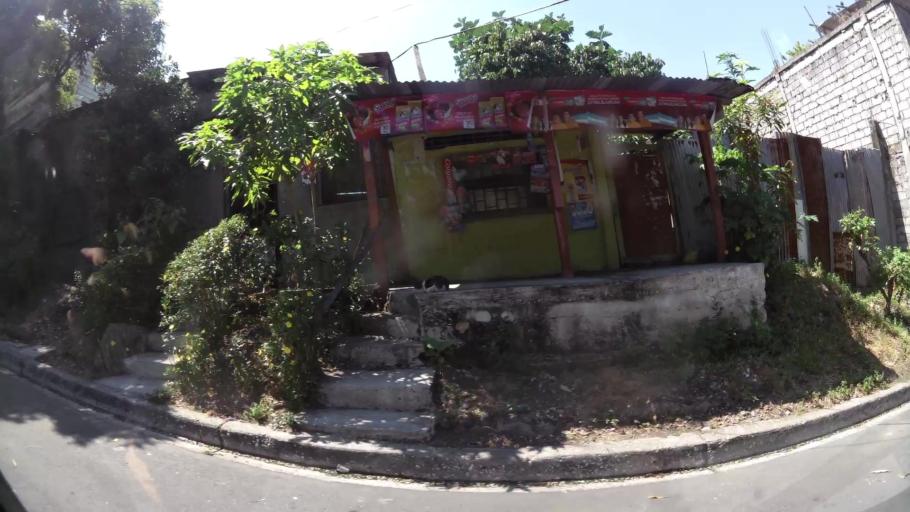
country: EC
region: Guayas
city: Guayaquil
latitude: -2.1854
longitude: -79.9283
